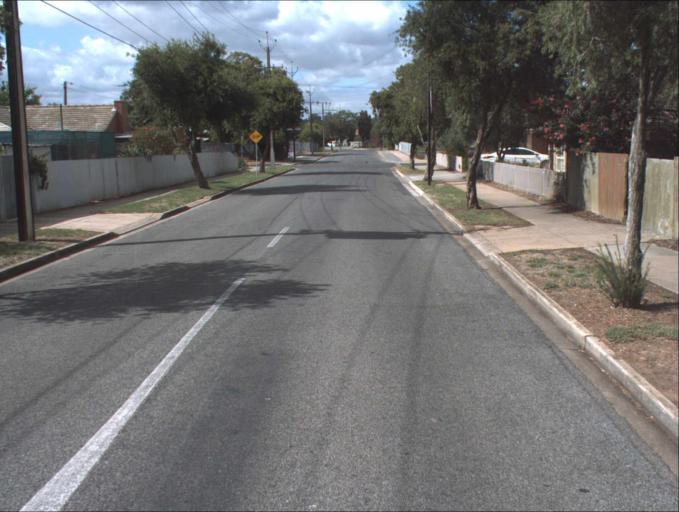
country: AU
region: South Australia
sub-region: Port Adelaide Enfield
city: Blair Athol
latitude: -34.8592
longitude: 138.5941
